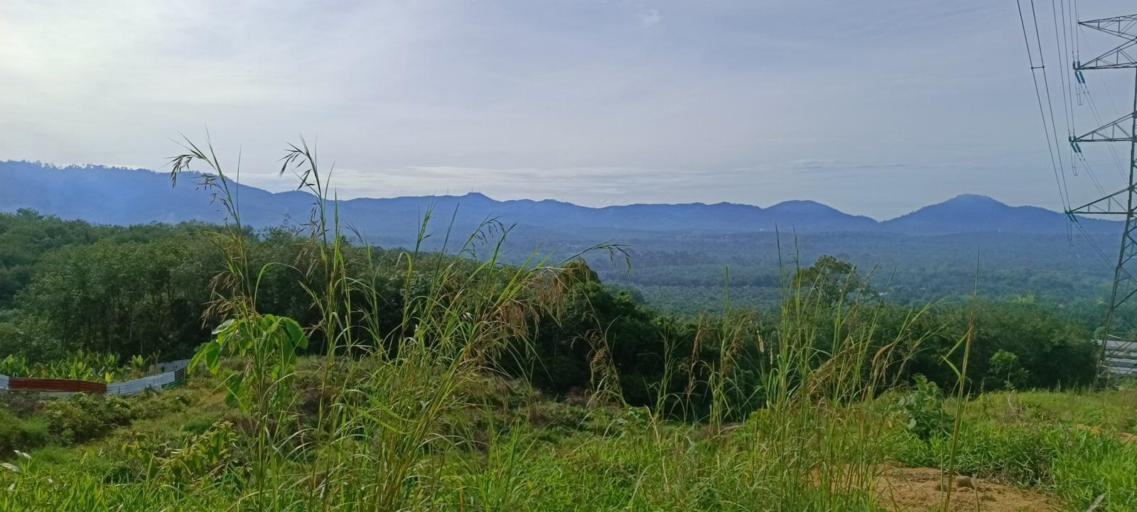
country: MY
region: Penang
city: Nibong Tebal
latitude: 5.2216
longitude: 100.5162
